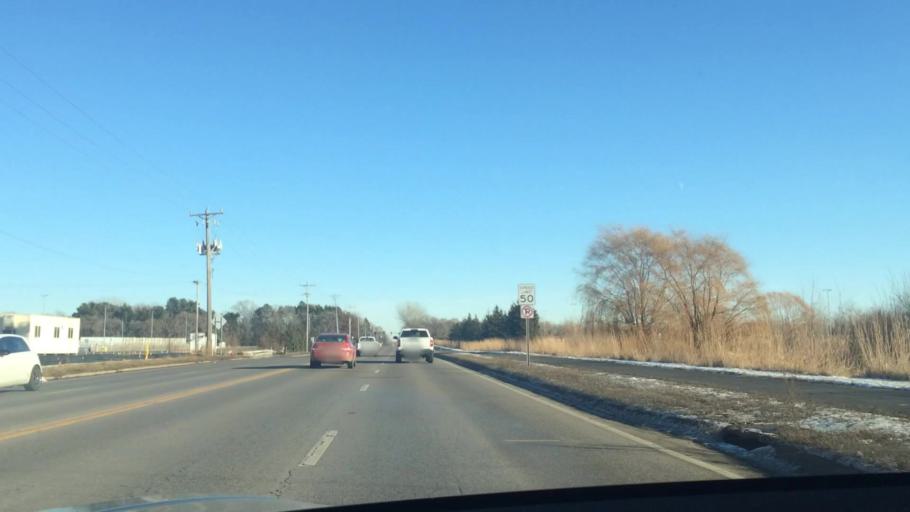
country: US
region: Minnesota
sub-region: Anoka County
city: Lexington
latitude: 45.1243
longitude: -93.1786
